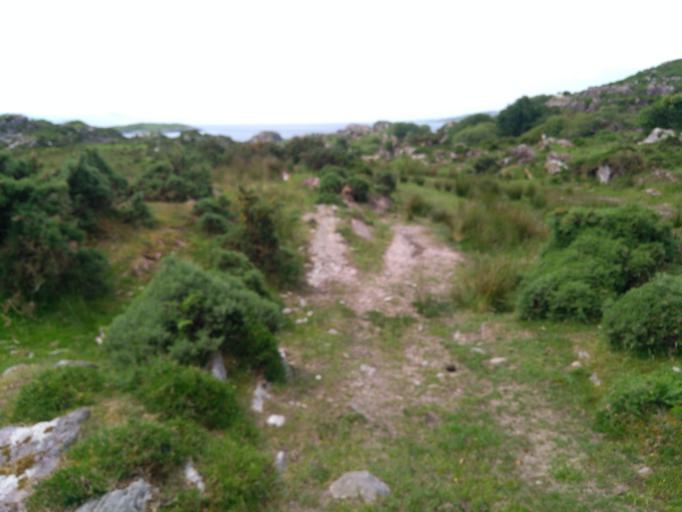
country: IE
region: Munster
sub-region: Ciarrai
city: Cahersiveen
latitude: 51.8030
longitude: -9.9354
